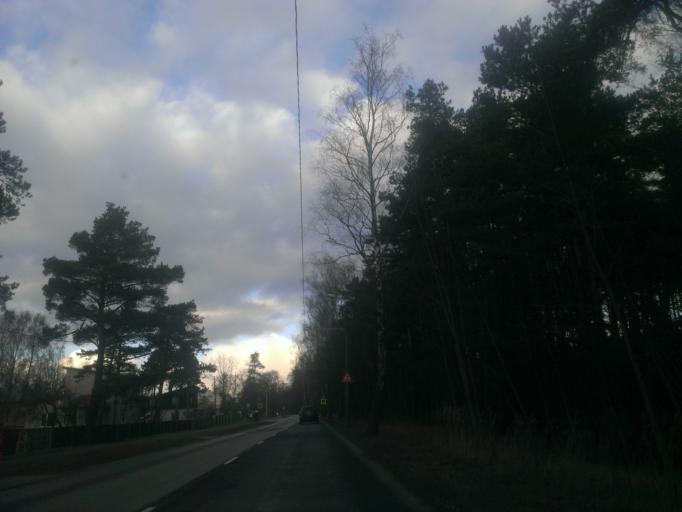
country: LV
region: Riga
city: Bolderaja
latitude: 57.0580
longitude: 24.1054
